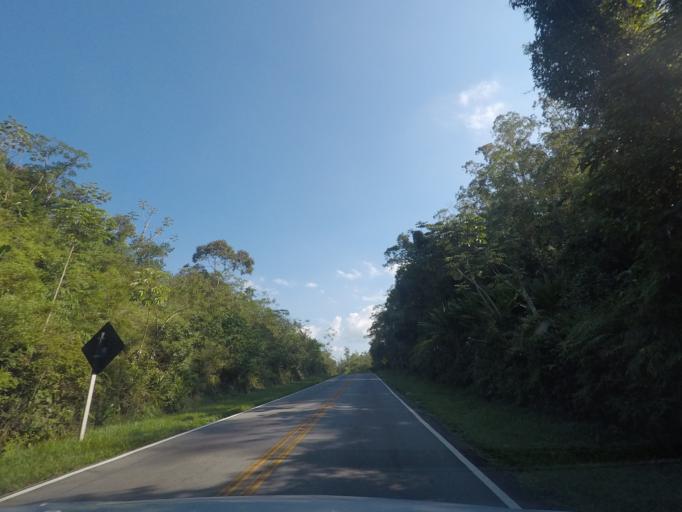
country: BR
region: Parana
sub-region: Antonina
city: Antonina
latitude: -25.5240
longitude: -48.7721
